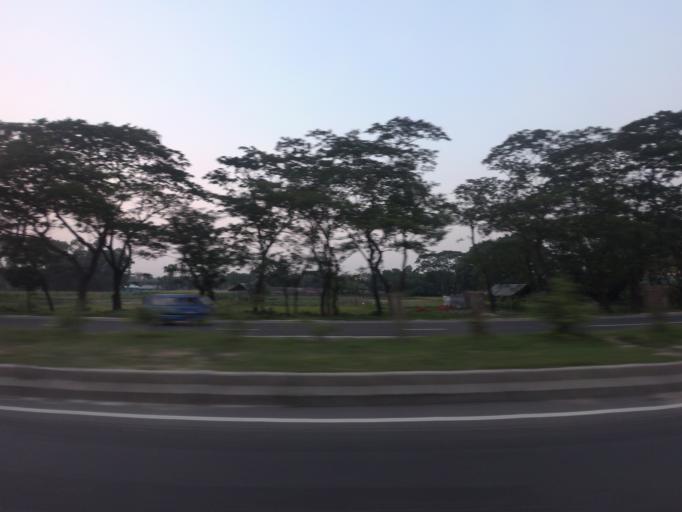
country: BD
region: Chittagong
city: Comilla
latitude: 23.4826
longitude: 91.0306
